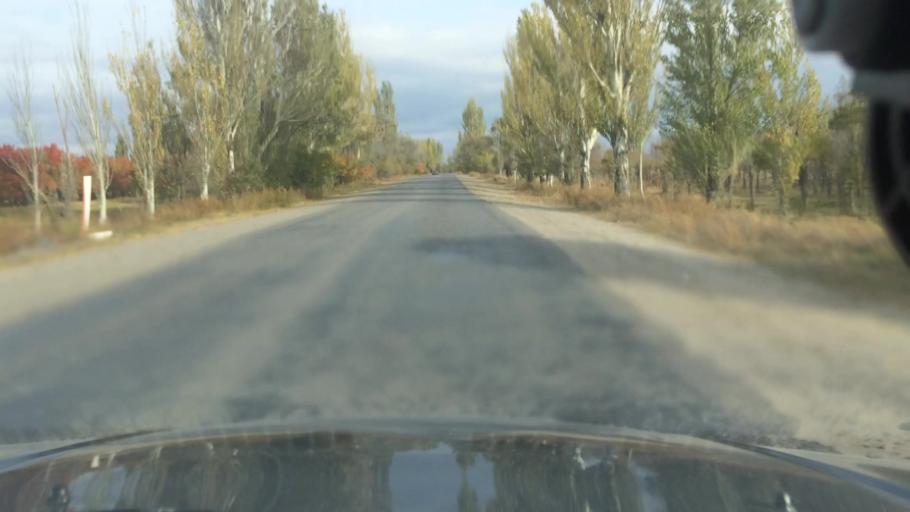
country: KG
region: Ysyk-Koel
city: Karakol
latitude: 42.5695
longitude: 78.3910
